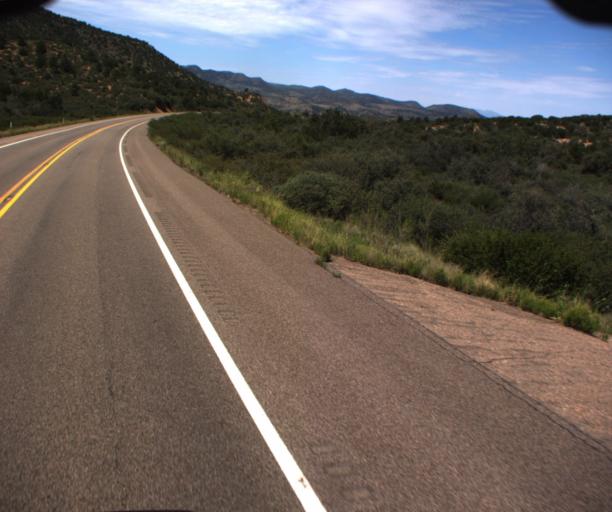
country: US
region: Arizona
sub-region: Gila County
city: Globe
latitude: 33.6135
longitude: -110.6084
